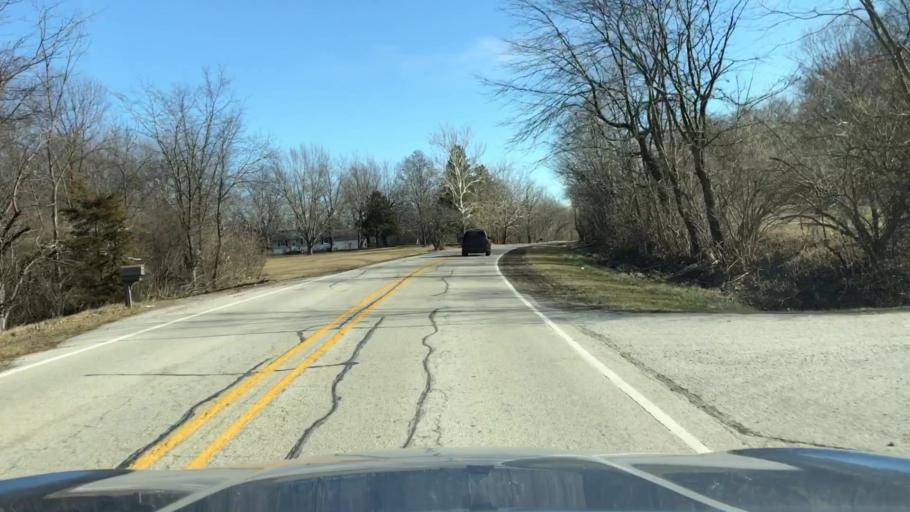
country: US
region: Illinois
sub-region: McLean County
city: Lexington
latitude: 40.6476
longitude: -88.8409
